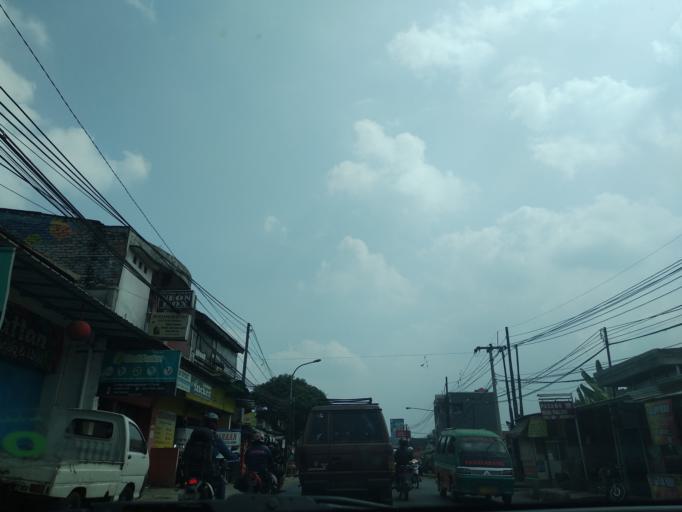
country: ID
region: West Java
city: Cimahi
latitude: -6.8685
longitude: 107.5244
